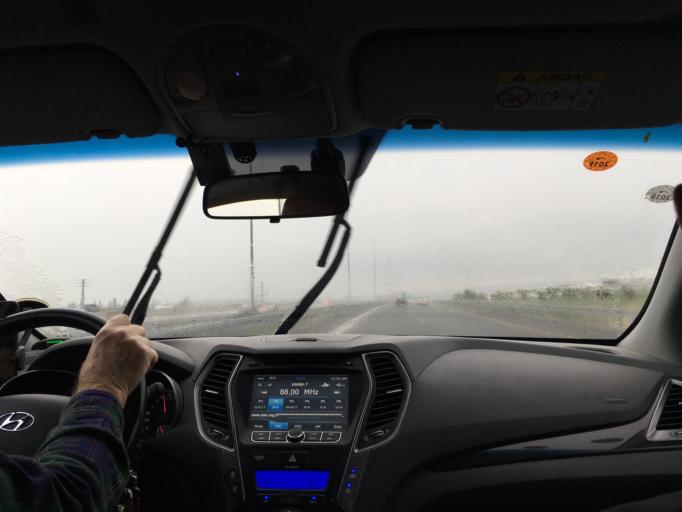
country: IL
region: Central District
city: Rosh Ha'Ayin
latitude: 32.1203
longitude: 34.9412
